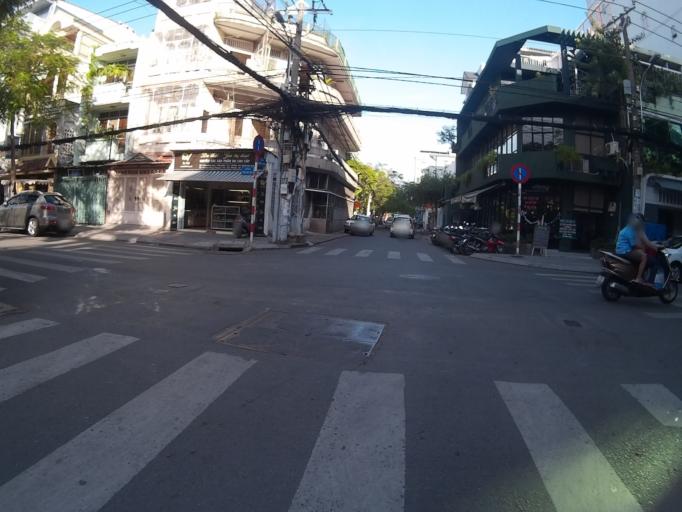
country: VN
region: Ho Chi Minh City
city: Quan Binh Thanh
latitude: 10.7925
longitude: 106.6895
